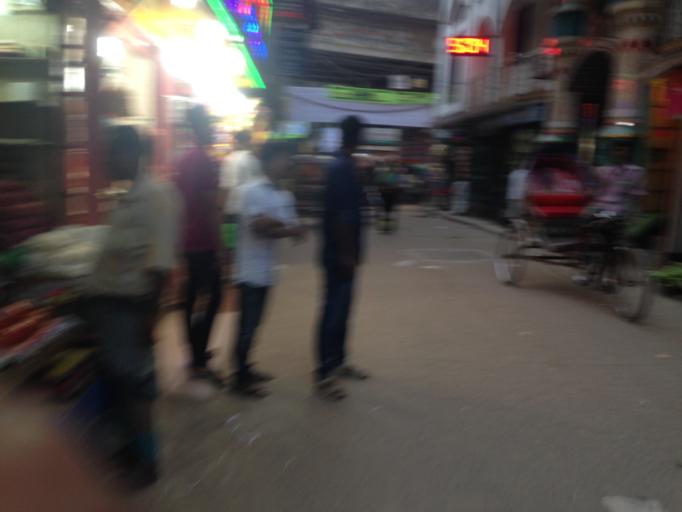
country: BD
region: Dhaka
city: Paltan
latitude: 23.7441
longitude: 90.4242
